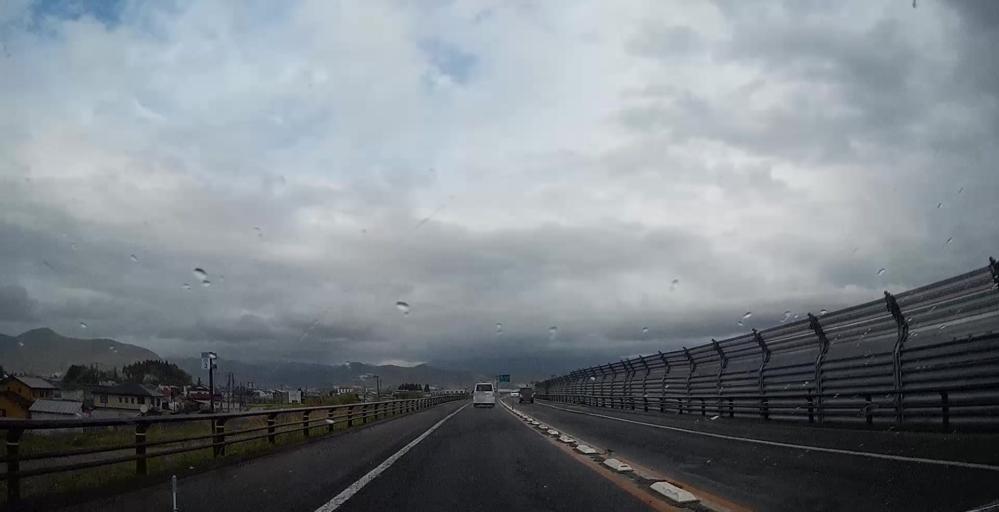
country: JP
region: Yamagata
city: Takahata
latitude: 38.0354
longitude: 140.1507
